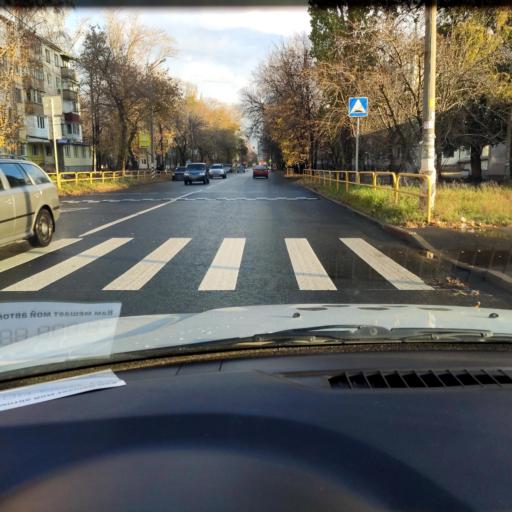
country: RU
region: Samara
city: Tol'yatti
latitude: 53.5161
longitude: 49.4243
